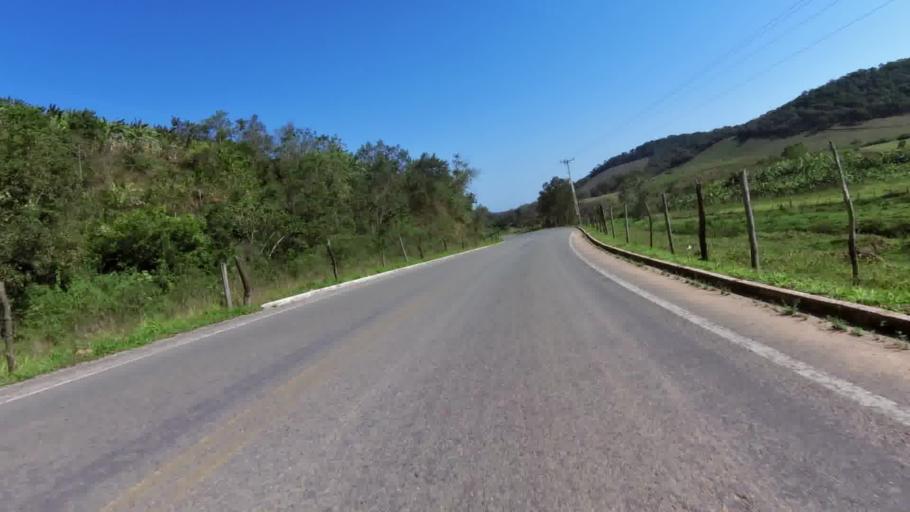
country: BR
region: Espirito Santo
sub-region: Alfredo Chaves
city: Alfredo Chaves
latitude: -20.5446
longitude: -40.7872
